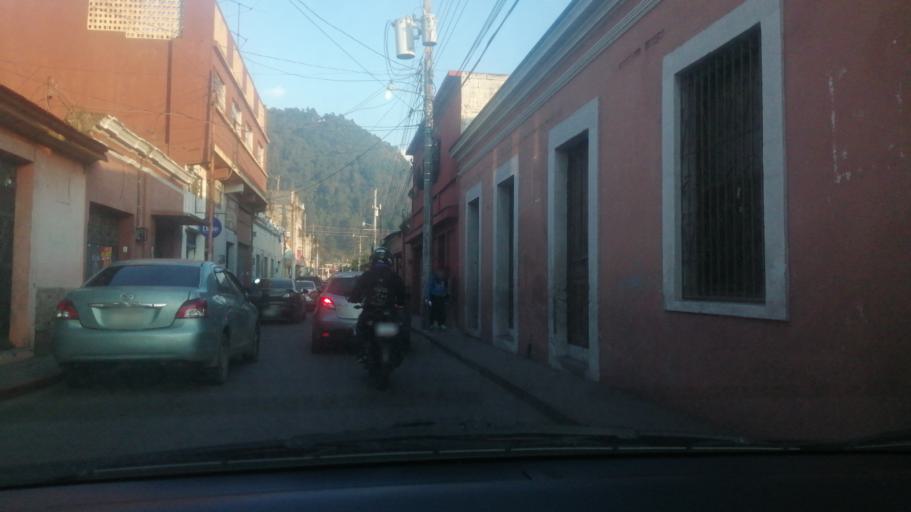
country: GT
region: Quetzaltenango
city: Quetzaltenango
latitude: 14.8326
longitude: -91.5142
